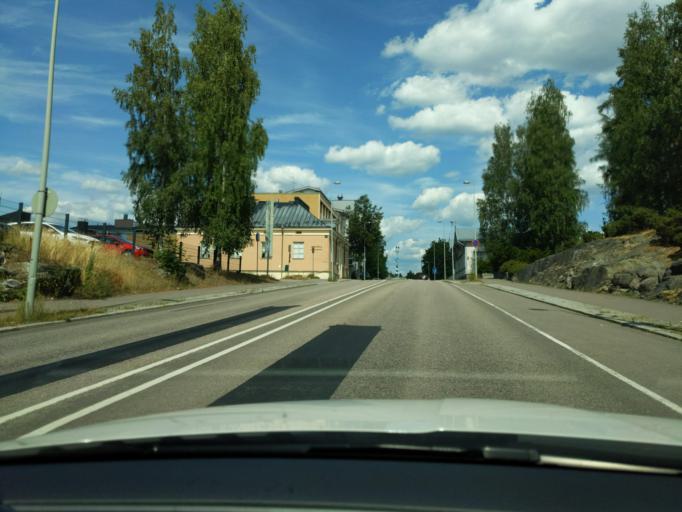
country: FI
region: Paijanne Tavastia
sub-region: Lahti
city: Heinola
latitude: 61.2016
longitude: 26.0360
